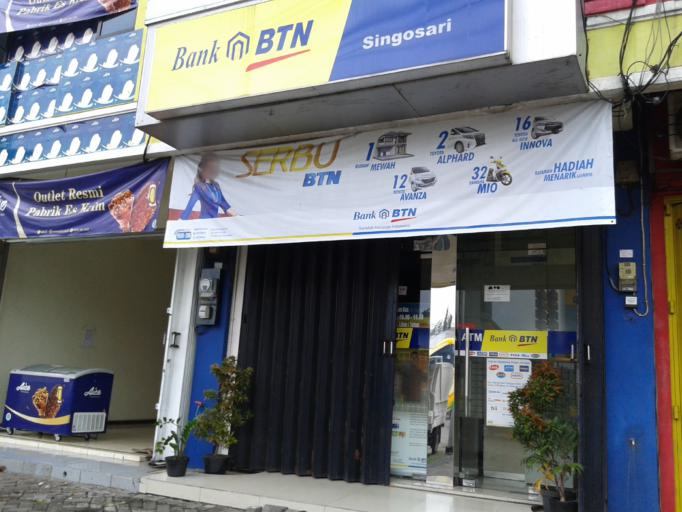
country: ID
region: East Java
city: Singosari
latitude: -7.8996
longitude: 112.6642
